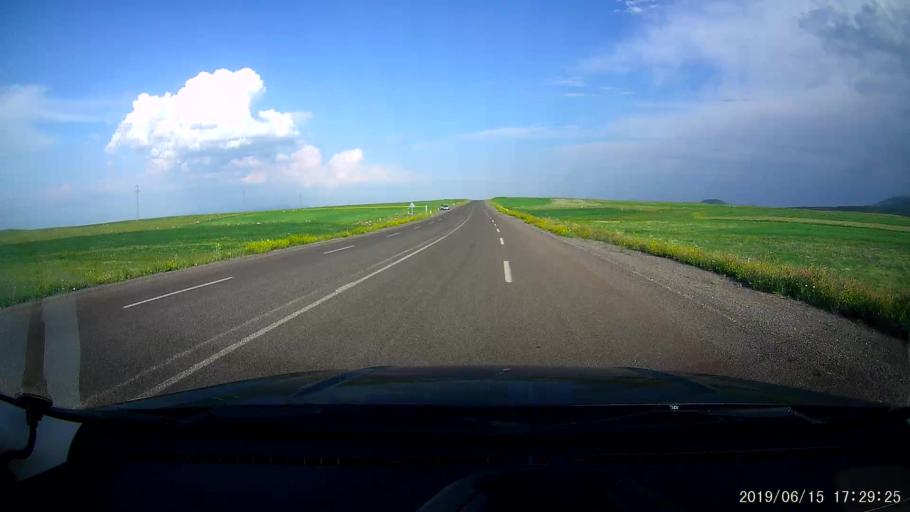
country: TR
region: Kars
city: Basgedikler
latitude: 40.5897
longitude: 43.4520
